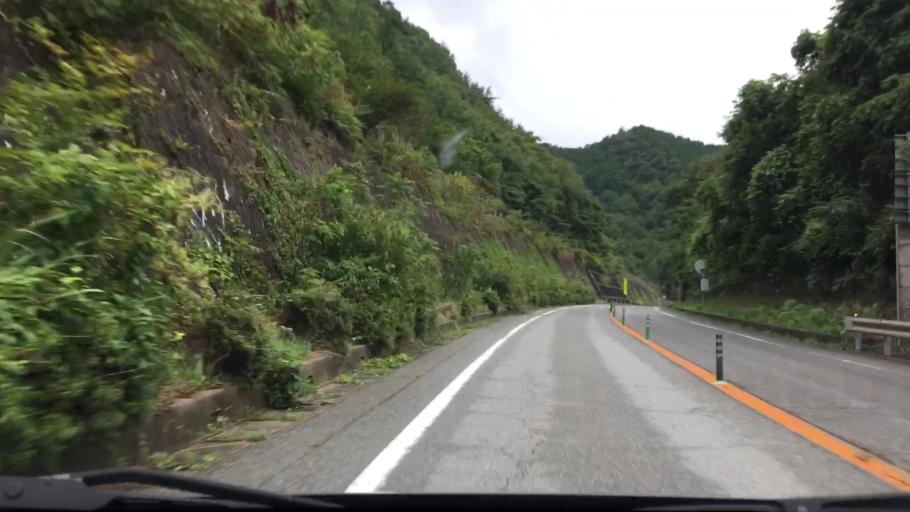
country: JP
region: Hyogo
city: Nishiwaki
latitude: 35.0379
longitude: 134.7700
